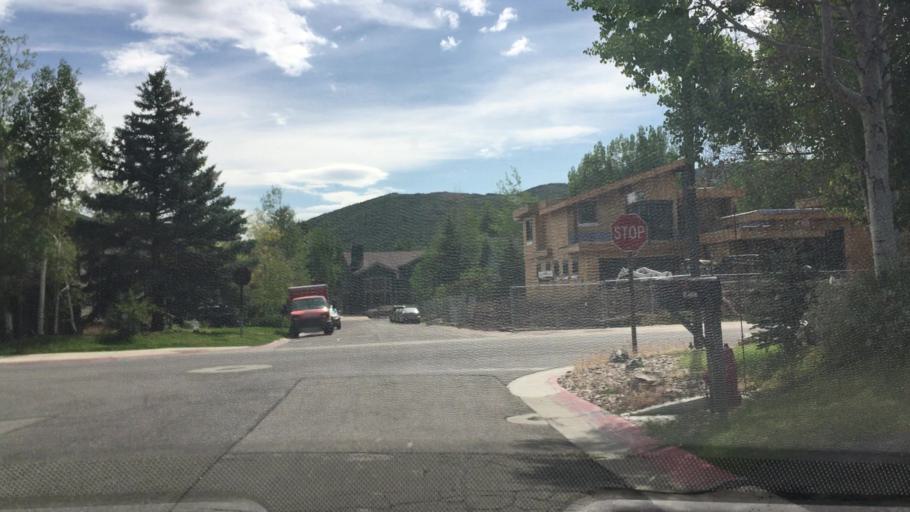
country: US
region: Utah
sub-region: Summit County
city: Park City
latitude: 40.6665
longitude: -111.4922
